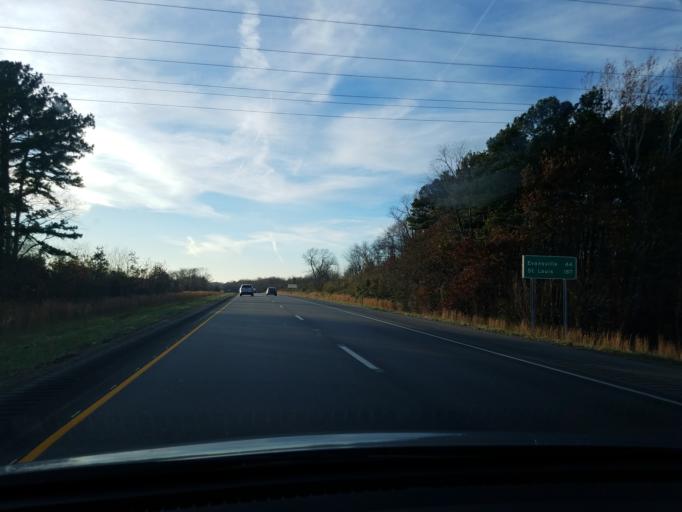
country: US
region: Indiana
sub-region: Spencer County
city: Dale
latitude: 38.1967
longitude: -86.9973
